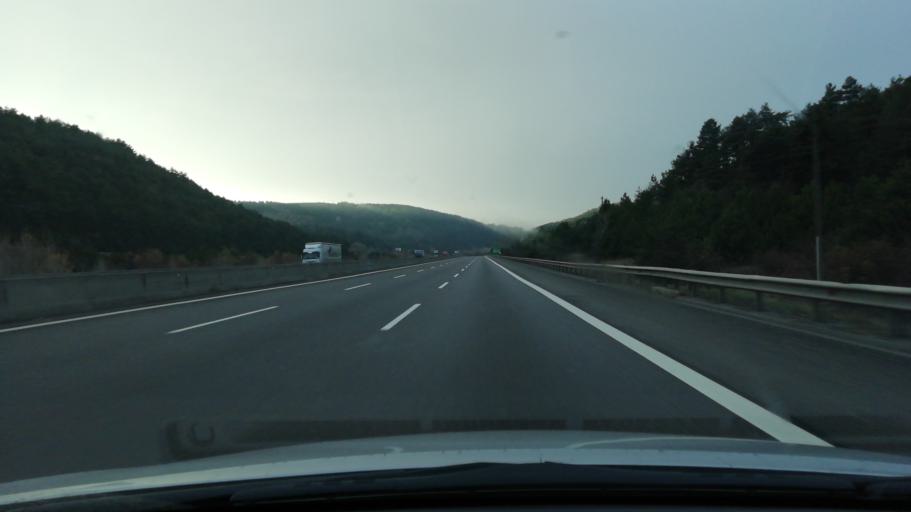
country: TR
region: Bolu
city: Bolu
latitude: 40.7360
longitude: 31.8007
